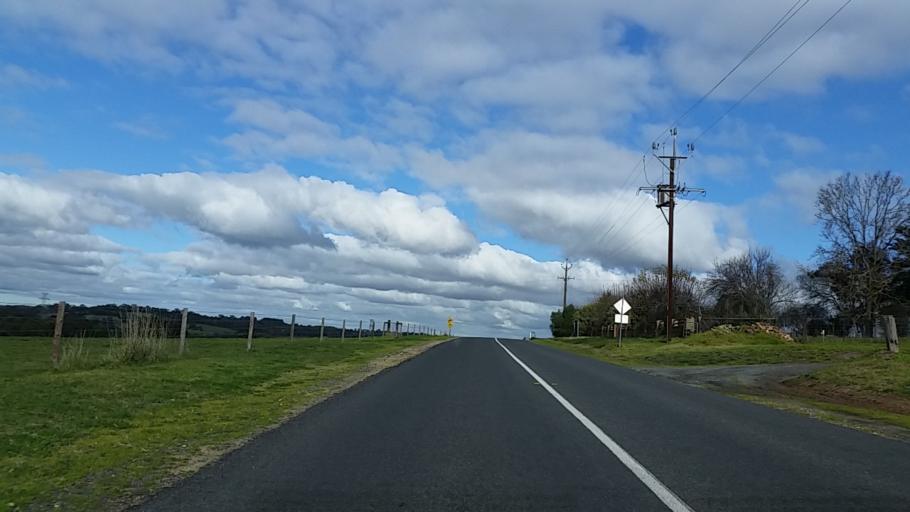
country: AU
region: South Australia
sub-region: Mount Barker
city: Little Hampton
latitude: -35.0754
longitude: 138.8337
